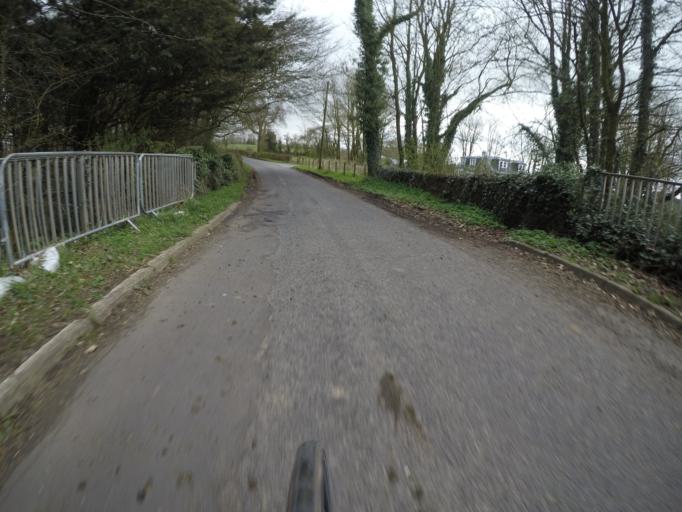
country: GB
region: Scotland
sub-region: East Ayrshire
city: Kilmaurs
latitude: 55.6702
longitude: -4.5693
